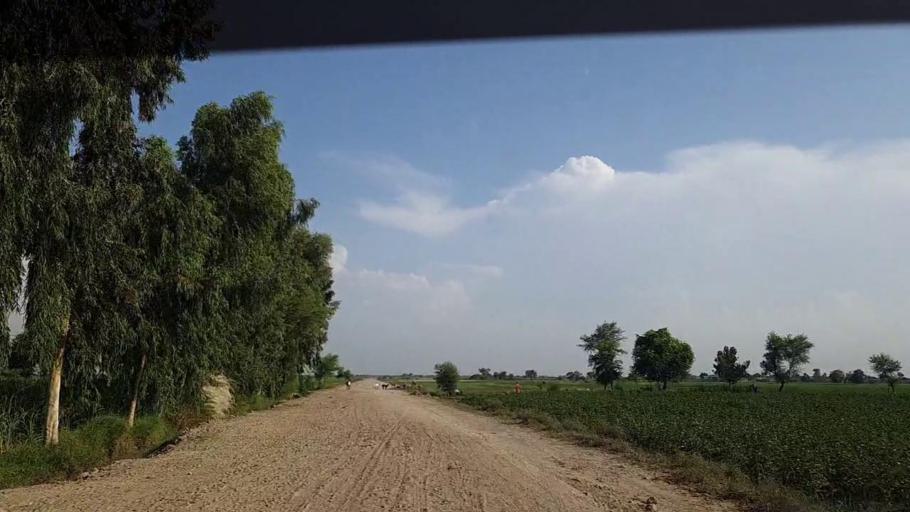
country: PK
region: Sindh
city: Khanpur
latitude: 27.8639
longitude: 69.3747
